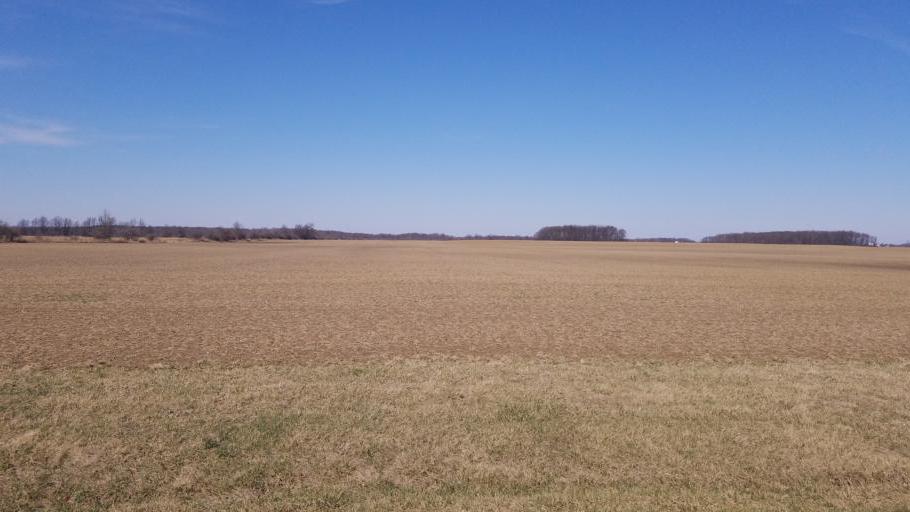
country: US
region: Ohio
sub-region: Hardin County
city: Kenton
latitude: 40.5414
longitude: -83.4551
